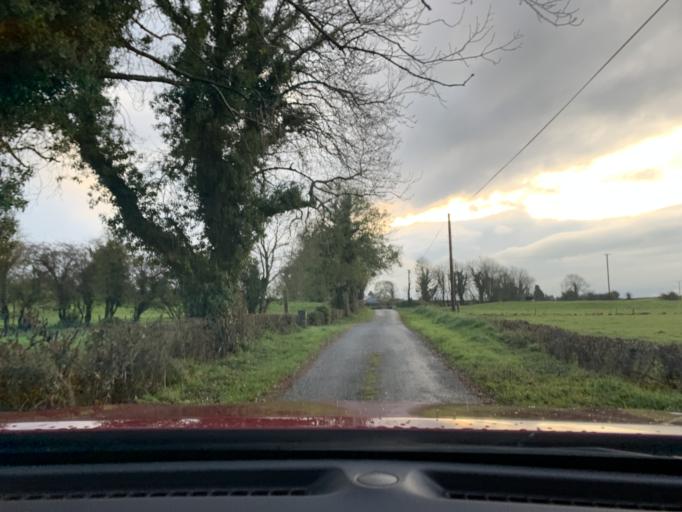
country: IE
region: Connaught
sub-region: Sligo
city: Ballymote
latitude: 54.0366
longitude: -8.5430
